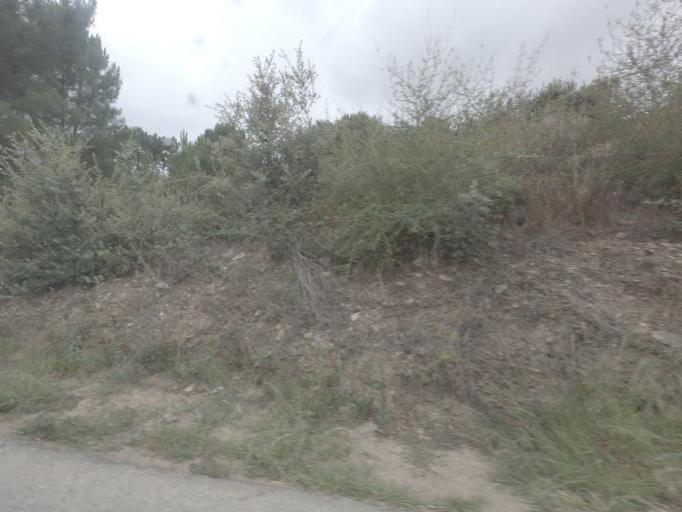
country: PT
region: Vila Real
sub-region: Sabrosa
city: Sabrosa
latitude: 41.2326
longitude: -7.4965
